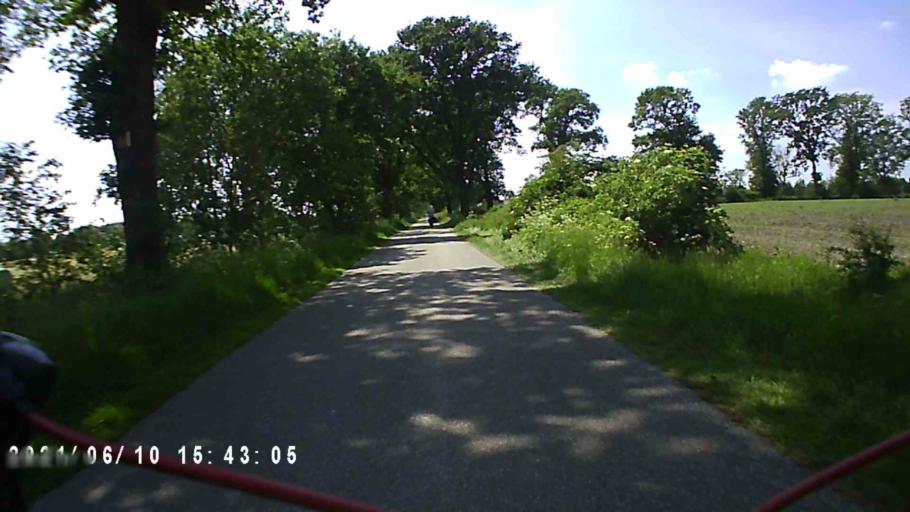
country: NL
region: Friesland
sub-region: Gemeente Achtkarspelen
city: Boelenslaan
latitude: 53.1673
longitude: 6.1414
